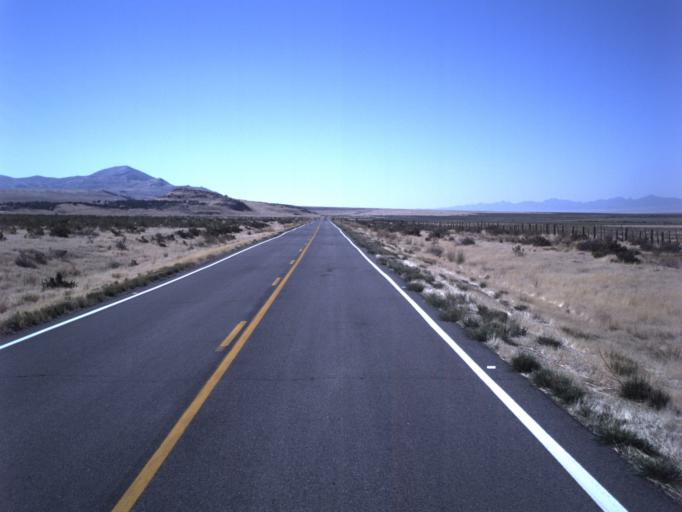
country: US
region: Utah
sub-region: Tooele County
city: Grantsville
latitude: 40.6293
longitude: -112.6959
